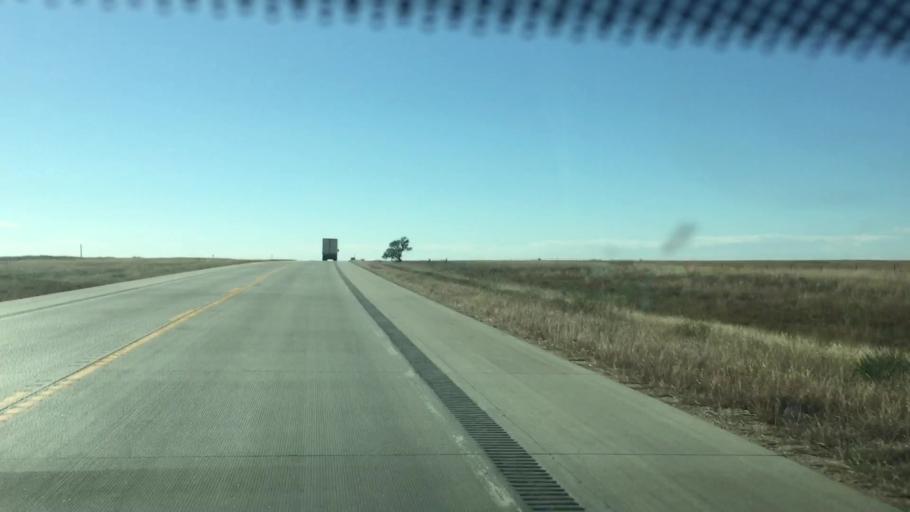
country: US
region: Colorado
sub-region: Kiowa County
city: Eads
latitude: 38.7639
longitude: -102.8232
